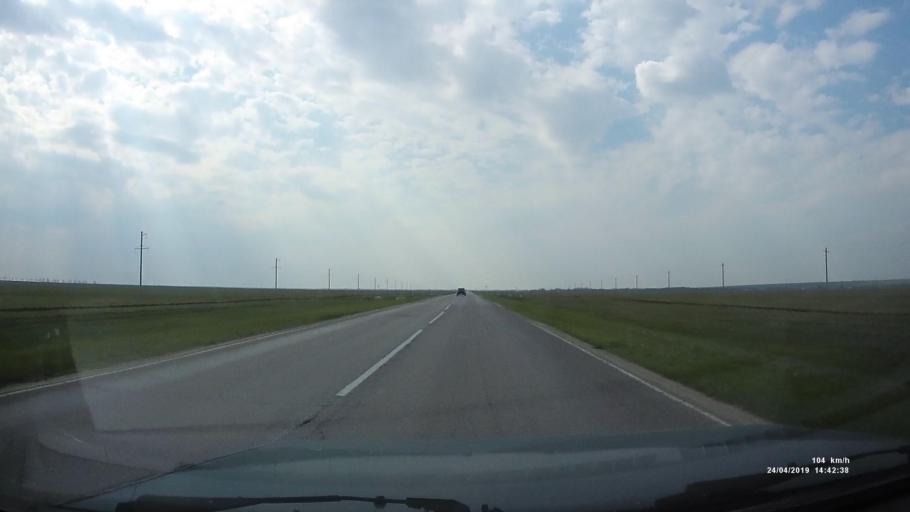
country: RU
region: Rostov
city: Remontnoye
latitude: 46.4531
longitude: 43.8579
